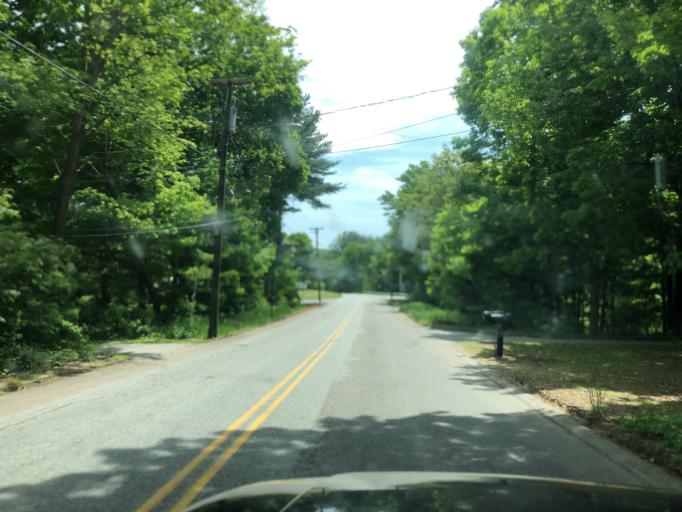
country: US
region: Connecticut
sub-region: Windham County
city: North Grosvenor Dale
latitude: 41.9761
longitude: -71.8870
